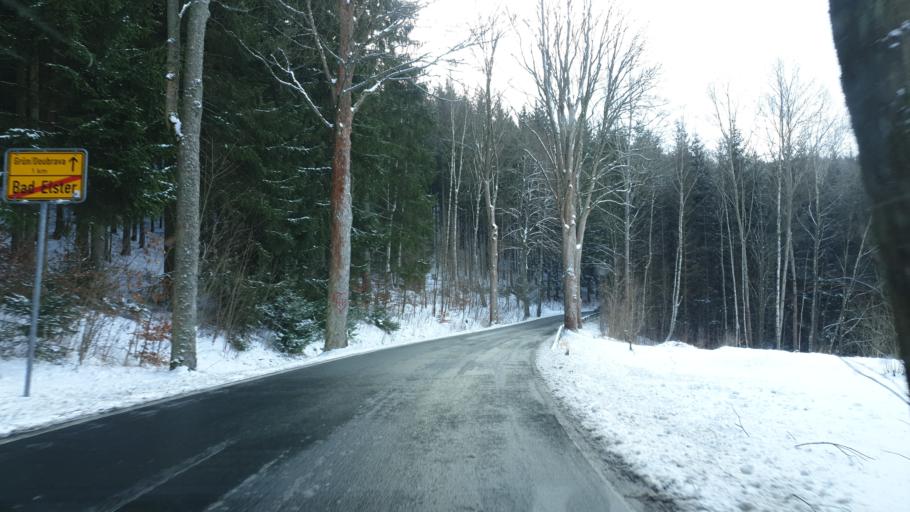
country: DE
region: Saxony
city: Bad Elster
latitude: 50.2715
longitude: 12.2495
